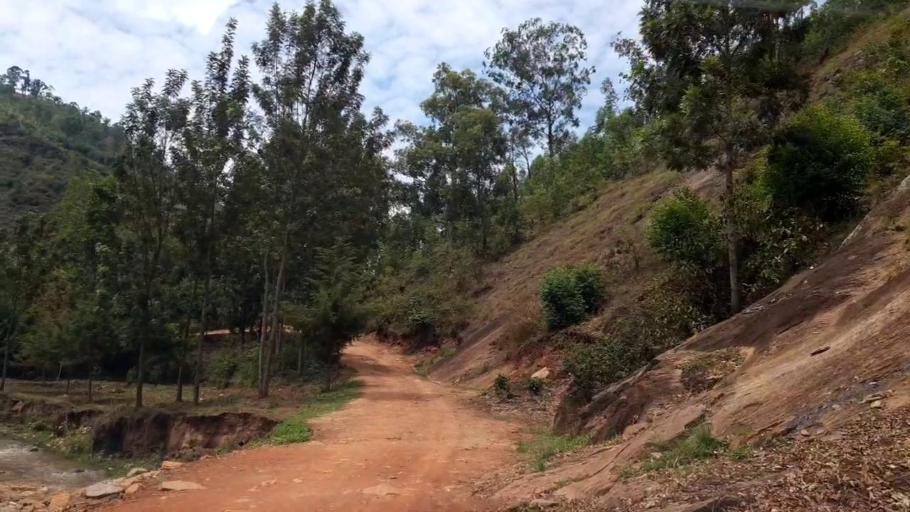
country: RW
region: Northern Province
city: Byumba
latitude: -1.5137
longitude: 30.1926
